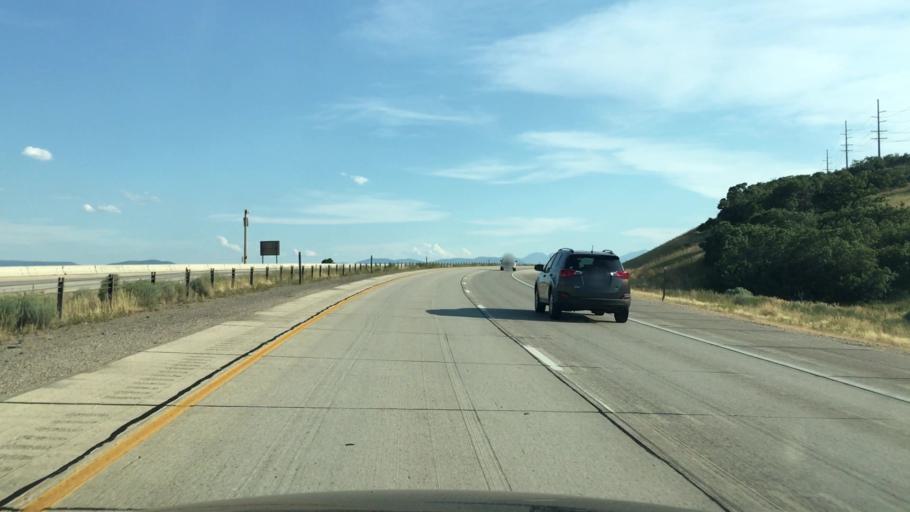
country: US
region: Utah
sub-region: Summit County
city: Park City
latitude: 40.6057
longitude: -111.4289
